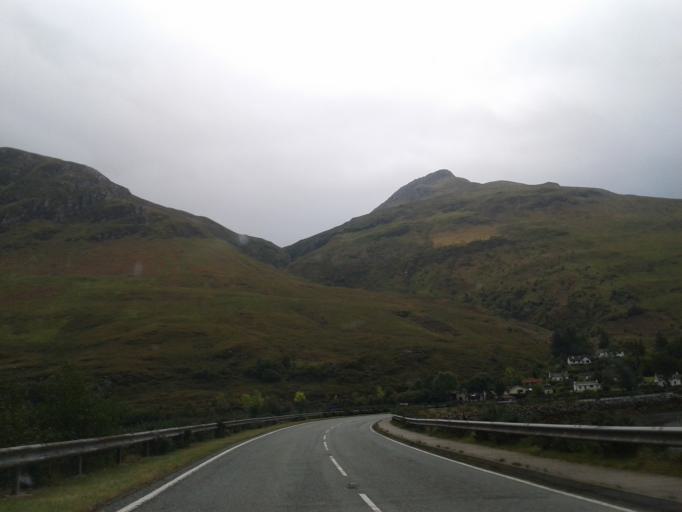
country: GB
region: Scotland
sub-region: Highland
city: Fort William
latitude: 57.2316
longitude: -5.4033
